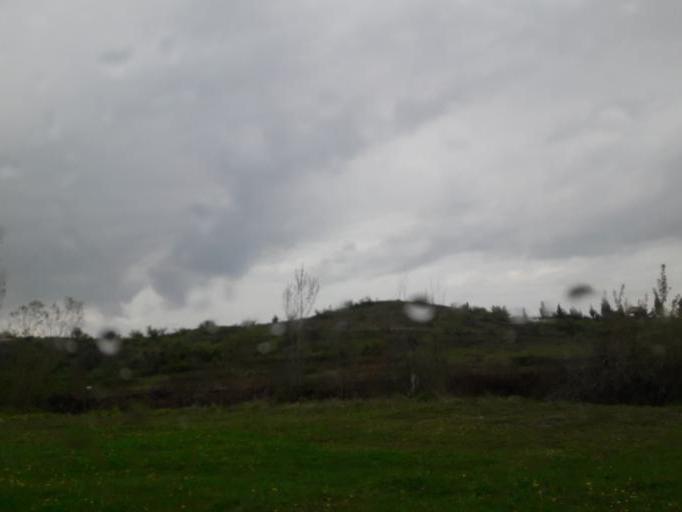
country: AL
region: Shkoder
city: Vukatane
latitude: 42.0103
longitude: 19.5476
